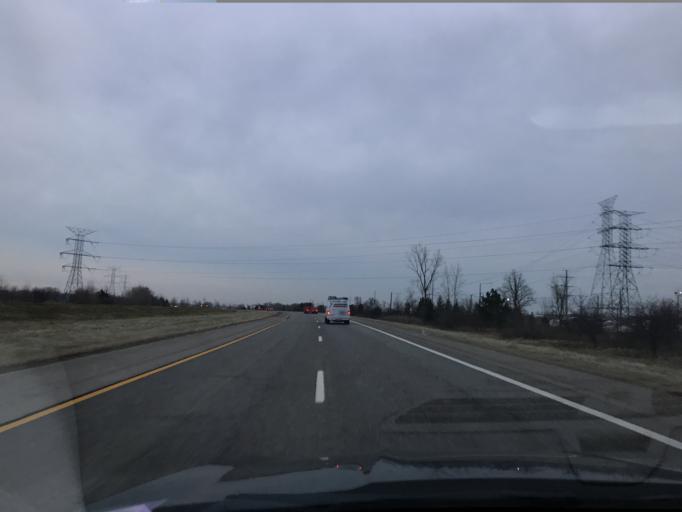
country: US
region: Michigan
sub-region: Macomb County
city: Romeo
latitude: 42.7816
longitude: -83.0086
